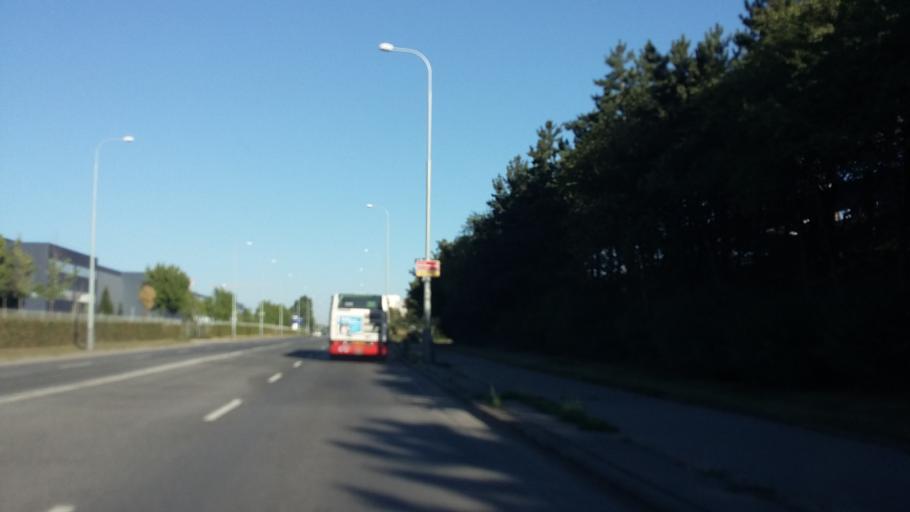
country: CZ
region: Praha
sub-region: Praha 18
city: Letnany
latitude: 50.1425
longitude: 14.5098
